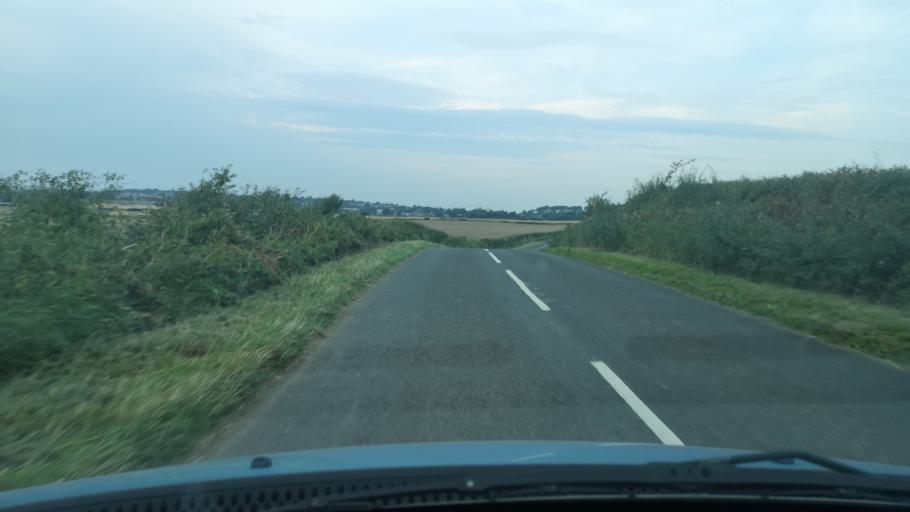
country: GB
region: England
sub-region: City and Borough of Wakefield
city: Darrington
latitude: 53.6631
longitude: -1.2862
